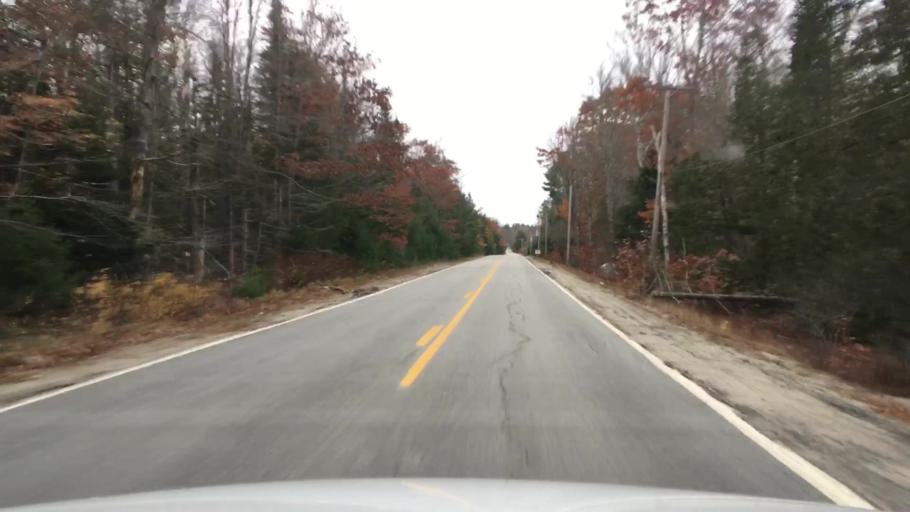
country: US
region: Maine
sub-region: Hancock County
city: Sedgwick
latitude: 44.3108
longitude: -68.5707
